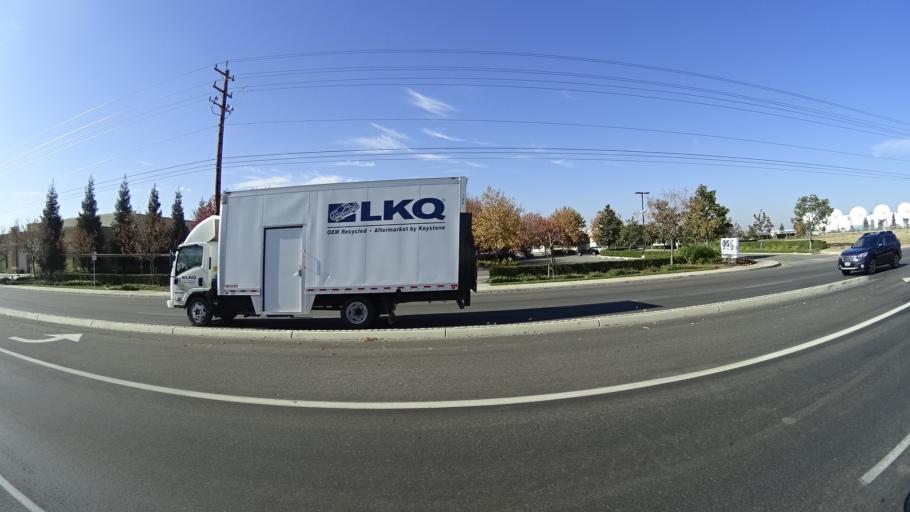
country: US
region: California
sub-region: Kern County
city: Greenfield
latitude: 35.3073
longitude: -119.0744
